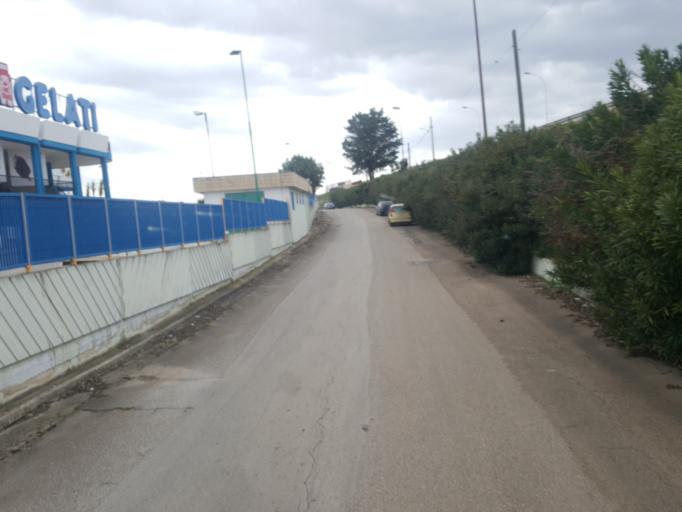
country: IT
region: Apulia
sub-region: Provincia di Bari
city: Conversano
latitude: 40.9774
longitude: 17.1090
